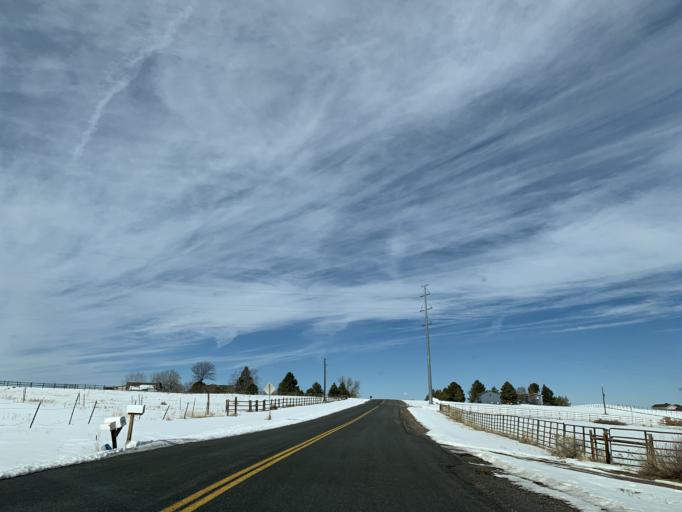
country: US
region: Colorado
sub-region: Douglas County
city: Carriage Club
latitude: 39.5154
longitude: -104.9030
